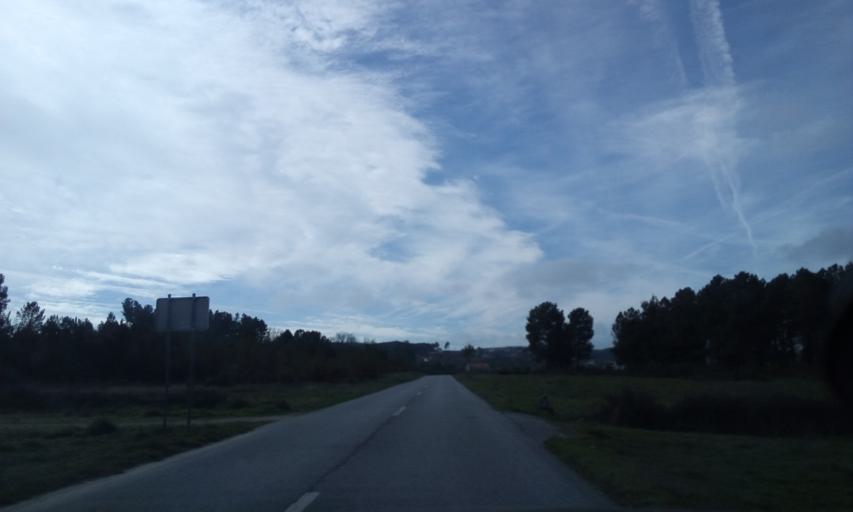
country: PT
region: Guarda
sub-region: Fornos de Algodres
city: Fornos de Algodres
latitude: 40.6644
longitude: -7.5304
